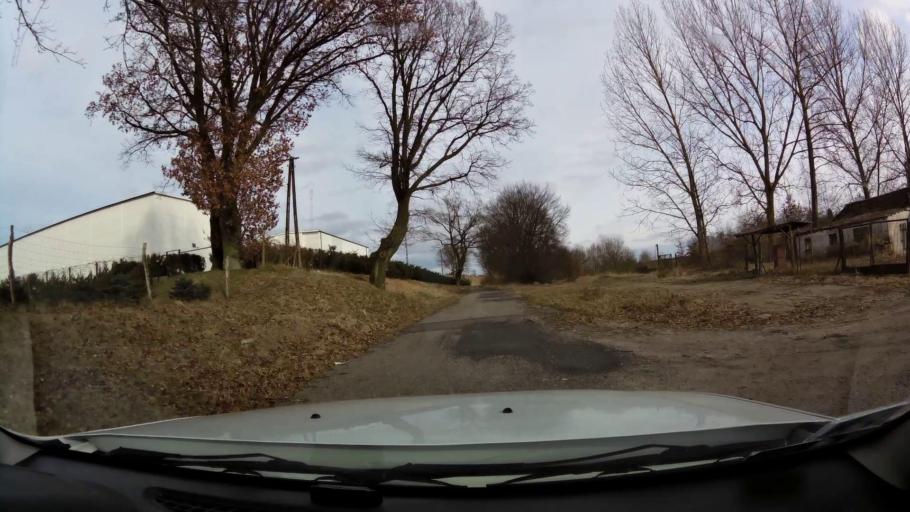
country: PL
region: West Pomeranian Voivodeship
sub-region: Powiat drawski
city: Drawsko Pomorskie
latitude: 53.5186
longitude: 15.7546
